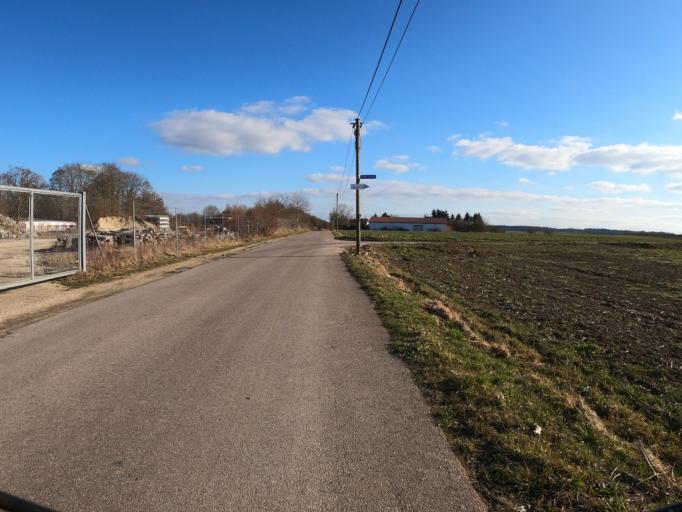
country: DE
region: Bavaria
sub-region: Swabia
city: Leipheim
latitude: 48.4422
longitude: 10.2077
